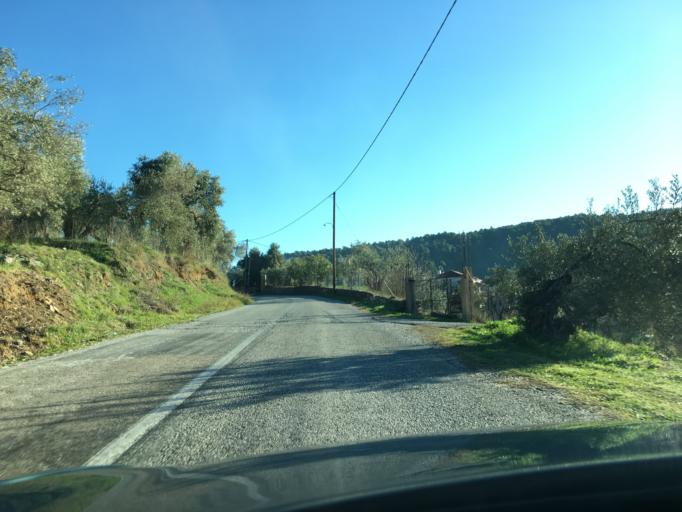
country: GR
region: Thessaly
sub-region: Nomos Magnisias
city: Skopelos
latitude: 39.0994
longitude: 23.6962
